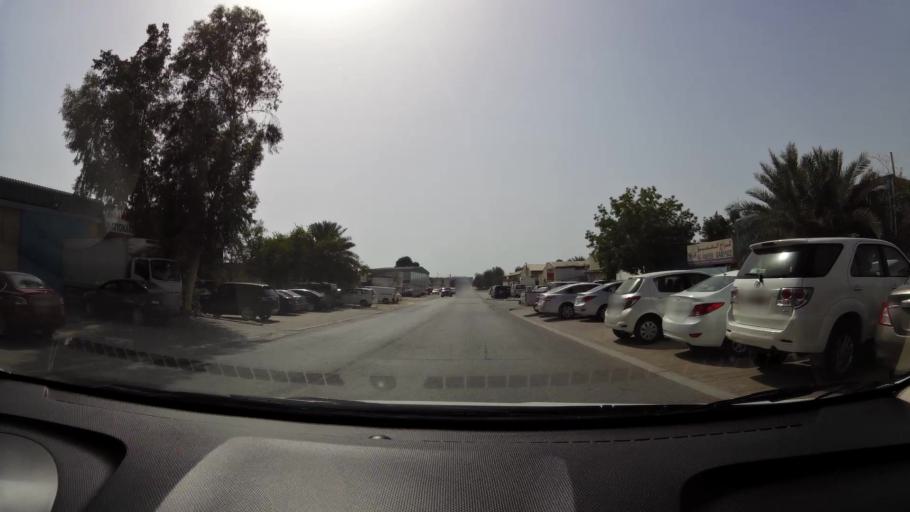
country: AE
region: Ash Shariqah
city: Sharjah
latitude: 25.2305
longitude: 55.3720
